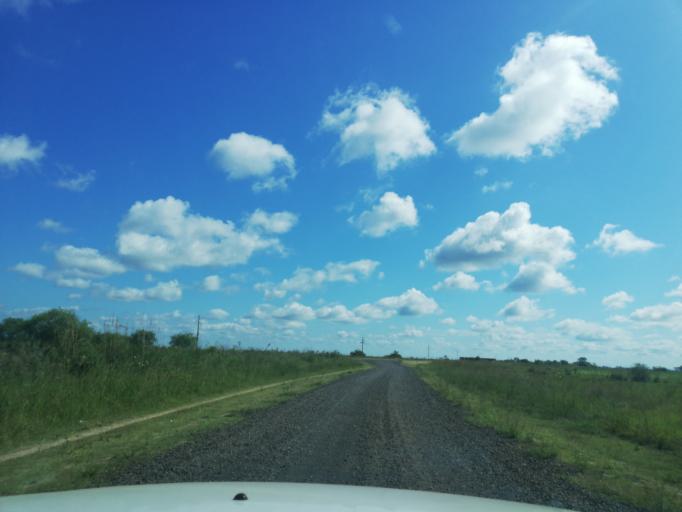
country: AR
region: Corrientes
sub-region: Departamento de San Miguel
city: San Miguel
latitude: -27.9731
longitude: -57.5804
